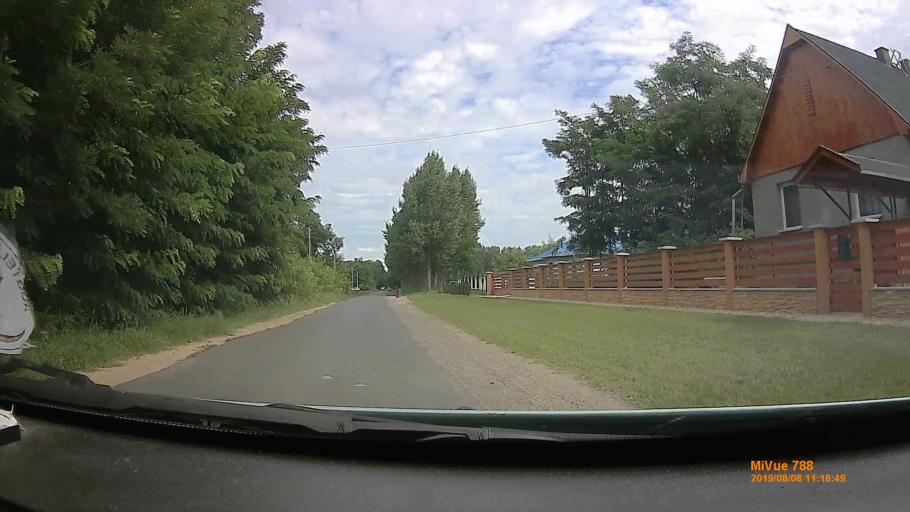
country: HU
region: Szabolcs-Szatmar-Bereg
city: Balkany
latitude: 47.7266
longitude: 21.8298
